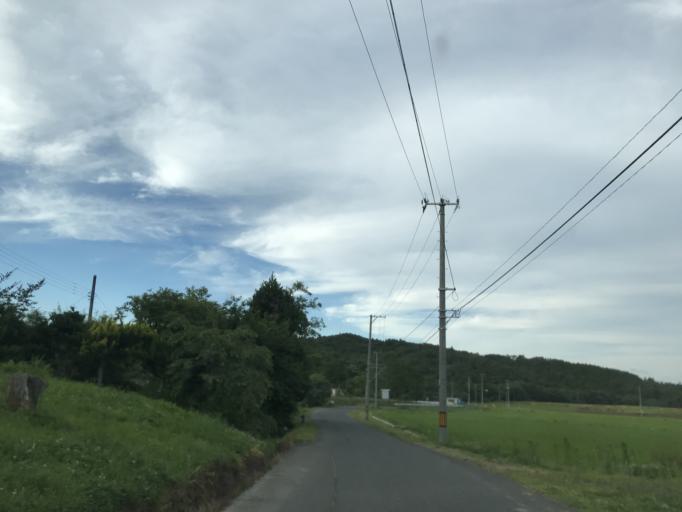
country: JP
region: Iwate
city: Ichinoseki
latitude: 38.9119
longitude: 141.0288
